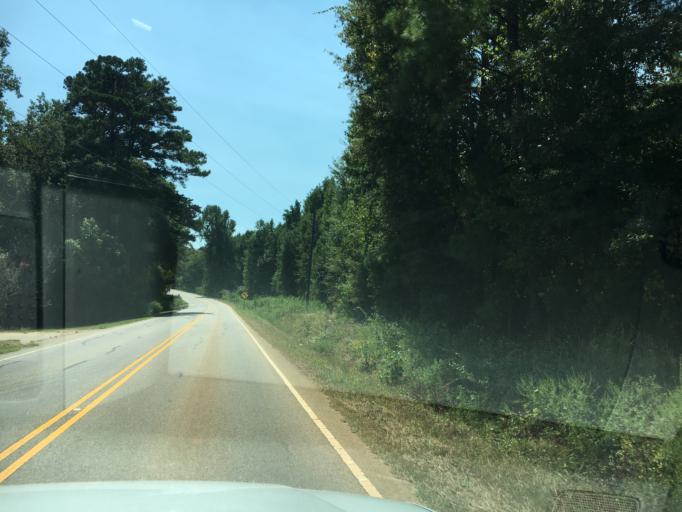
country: US
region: South Carolina
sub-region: Edgefield County
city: Johnston
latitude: 33.8539
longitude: -81.6788
